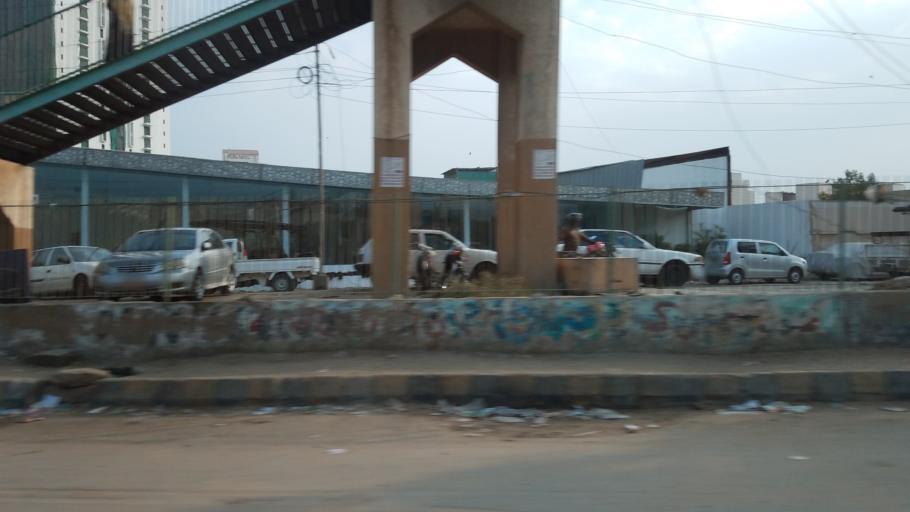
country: PK
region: Sindh
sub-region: Karachi District
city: Karachi
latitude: 24.9303
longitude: 67.0869
